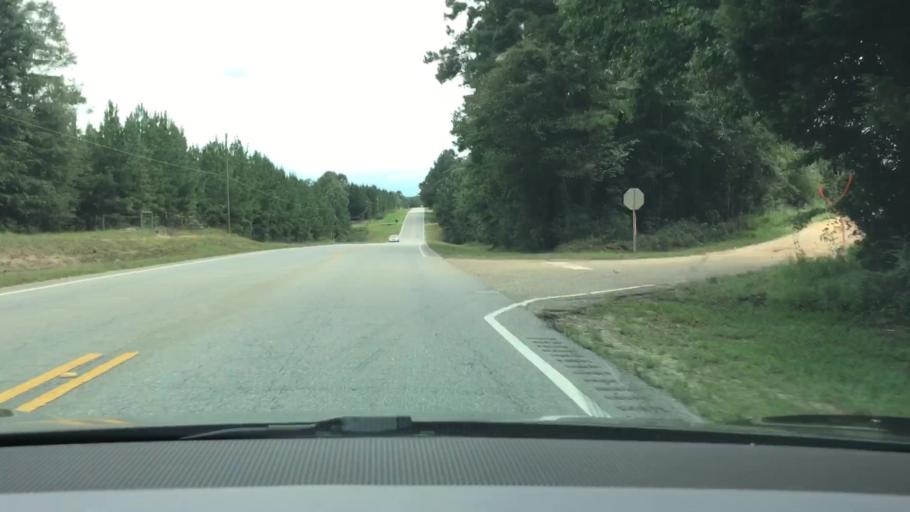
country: US
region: Alabama
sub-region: Pike County
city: Troy
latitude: 31.6343
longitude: -85.9729
